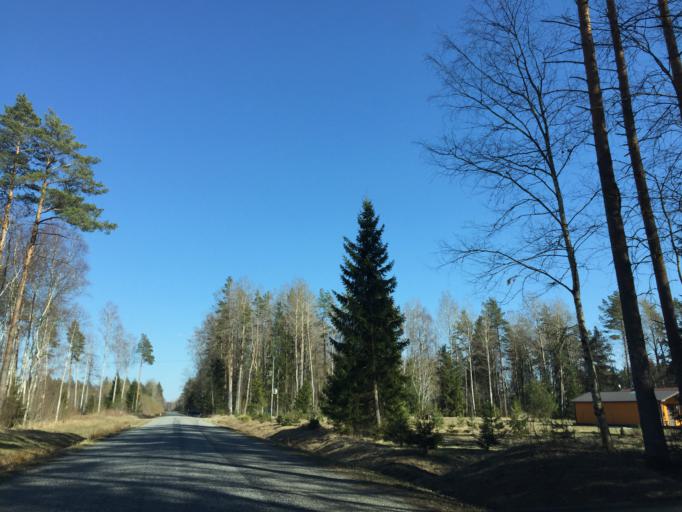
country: RU
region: Pskov
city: Gdov
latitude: 59.0109
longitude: 27.5719
